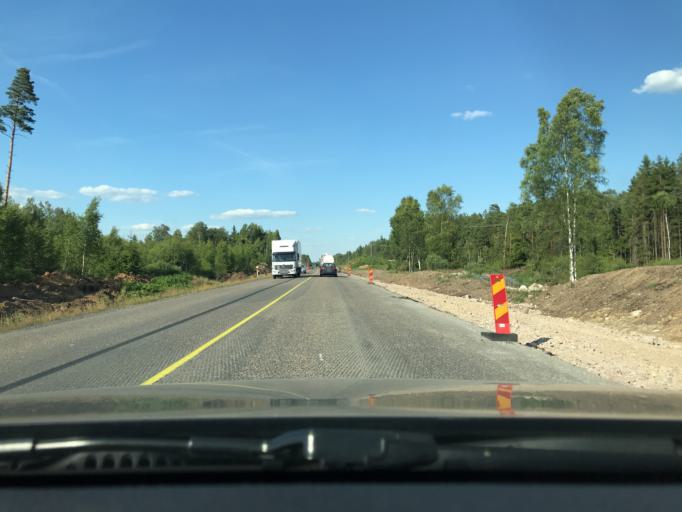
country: SE
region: Kronoberg
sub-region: Almhults Kommun
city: AElmhult
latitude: 56.5546
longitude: 14.1734
